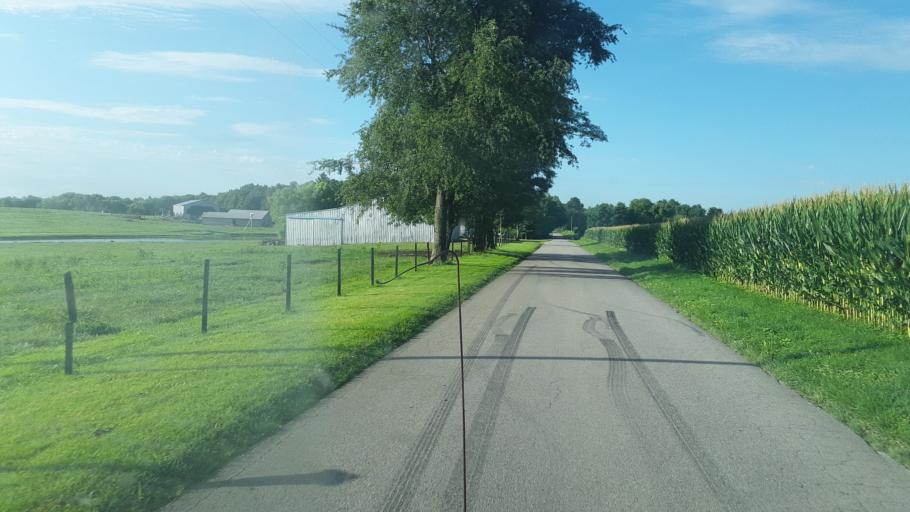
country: US
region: Kentucky
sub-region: Todd County
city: Guthrie
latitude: 36.6795
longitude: -87.1688
